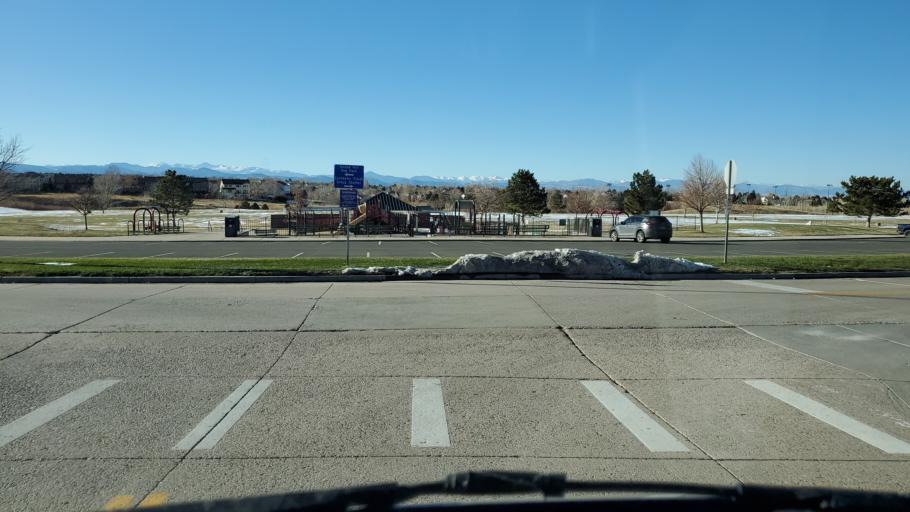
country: US
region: Colorado
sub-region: Douglas County
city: Carriage Club
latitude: 39.5391
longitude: -104.9165
